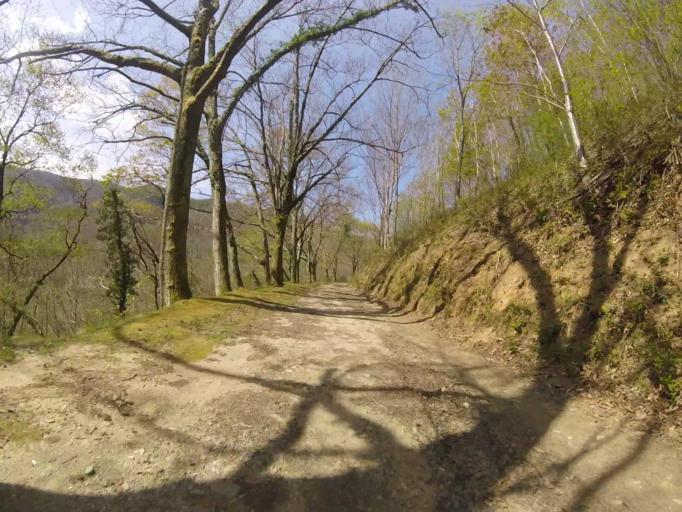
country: ES
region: Basque Country
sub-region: Provincia de Guipuzcoa
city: Irun
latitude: 43.2667
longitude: -1.8085
